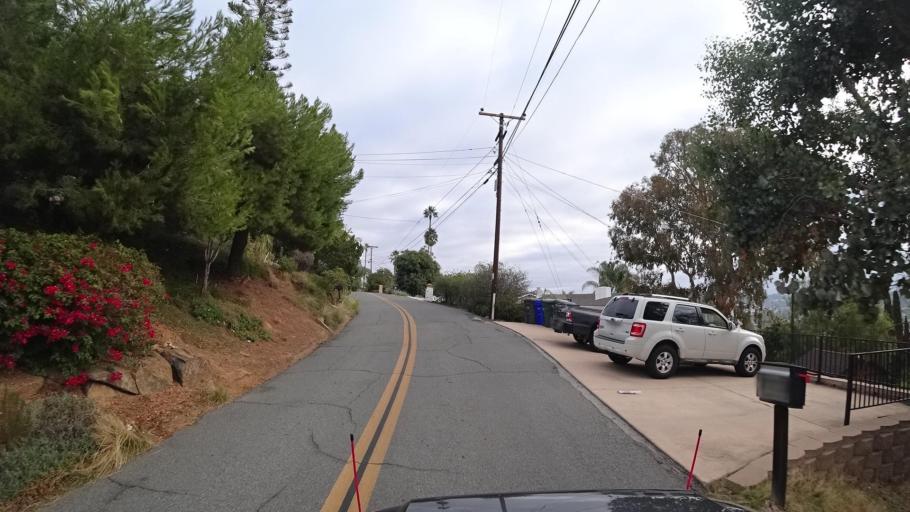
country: US
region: California
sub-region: San Diego County
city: Spring Valley
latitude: 32.7440
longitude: -117.0084
